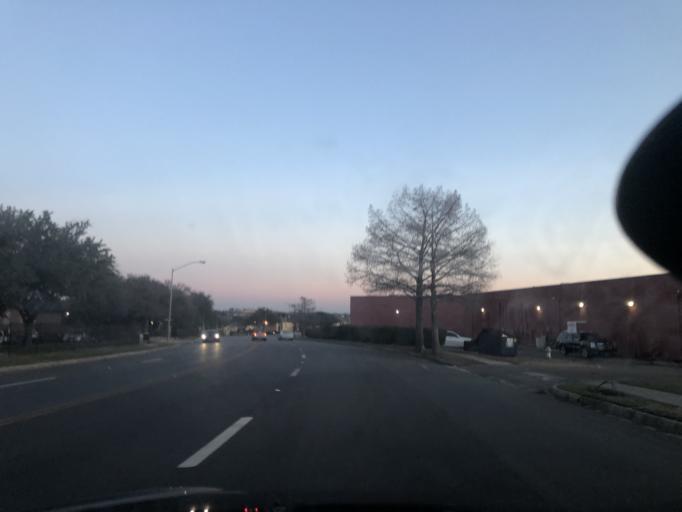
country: US
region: Texas
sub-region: Tarrant County
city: White Settlement
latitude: 32.7271
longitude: -97.4780
